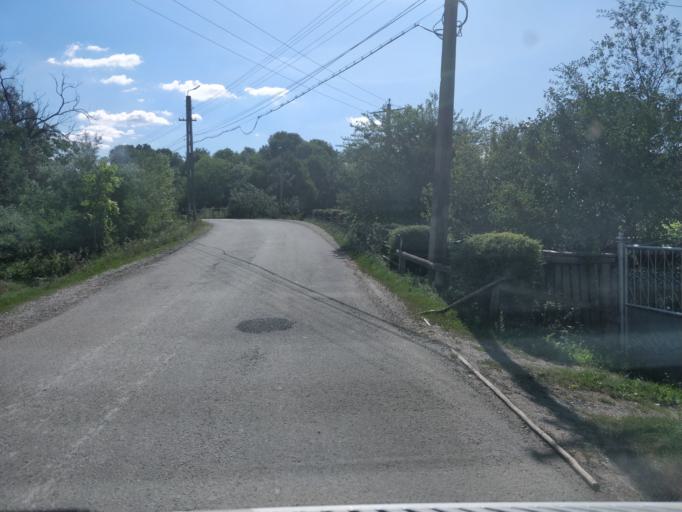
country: RO
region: Cluj
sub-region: Comuna Poeni
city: Poeni
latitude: 46.8924
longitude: 22.8773
